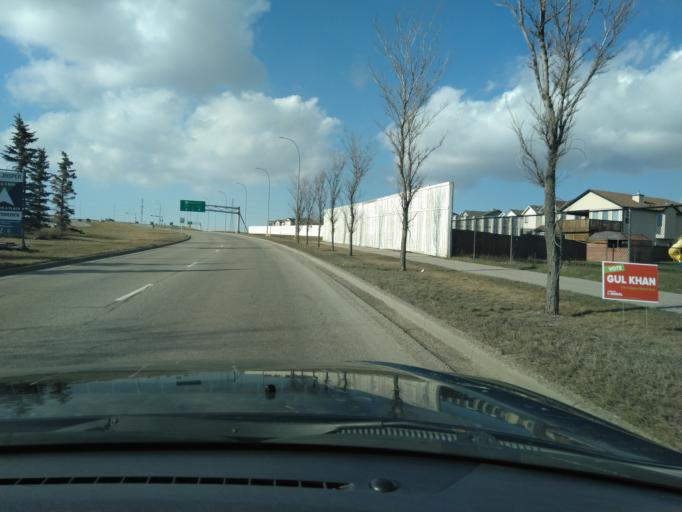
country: CA
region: Alberta
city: Calgary
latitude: 51.1682
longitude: -114.0676
